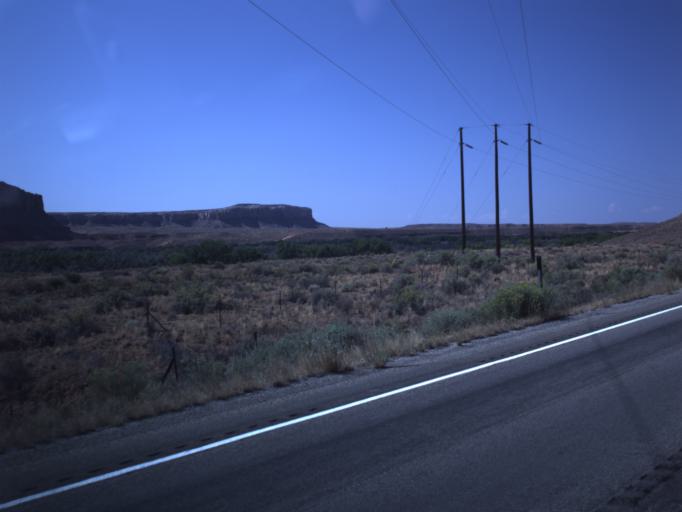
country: US
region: Utah
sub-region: San Juan County
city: Blanding
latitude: 37.2761
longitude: -109.5861
